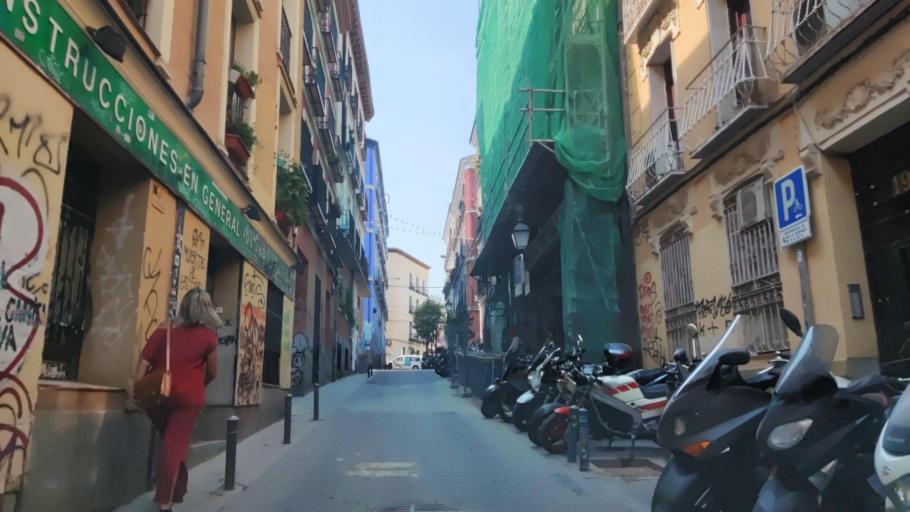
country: ES
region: Madrid
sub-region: Provincia de Madrid
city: Chamberi
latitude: 40.4263
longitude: -3.7049
